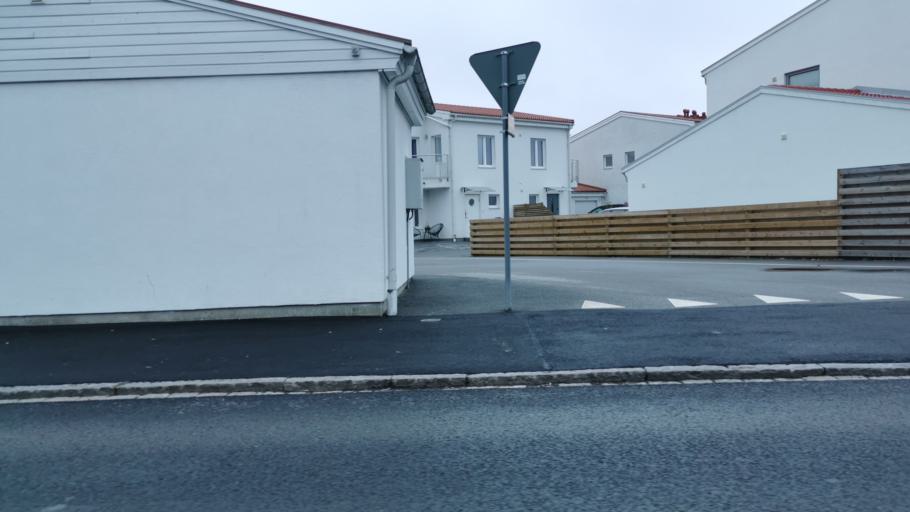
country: SE
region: Skane
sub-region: Burlovs Kommun
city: Arloev
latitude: 55.5899
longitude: 13.0809
